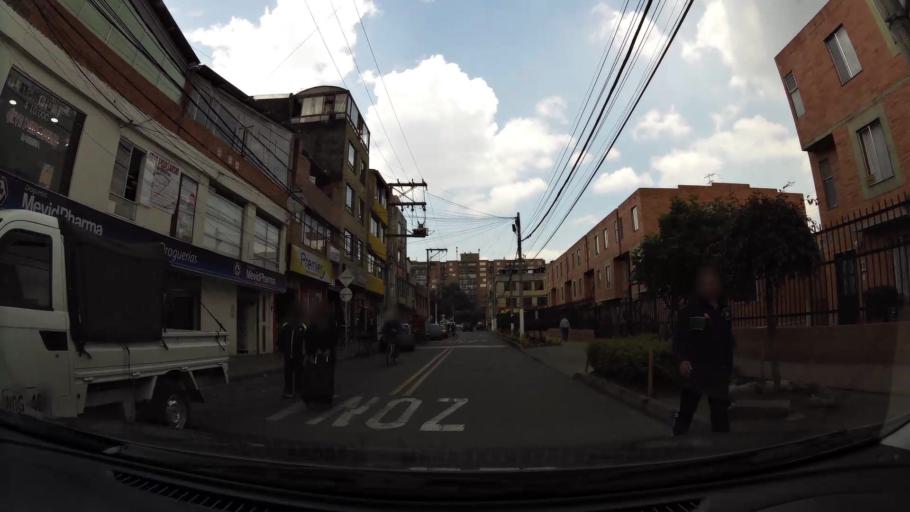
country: CO
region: Cundinamarca
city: Cota
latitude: 4.7427
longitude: -74.0587
